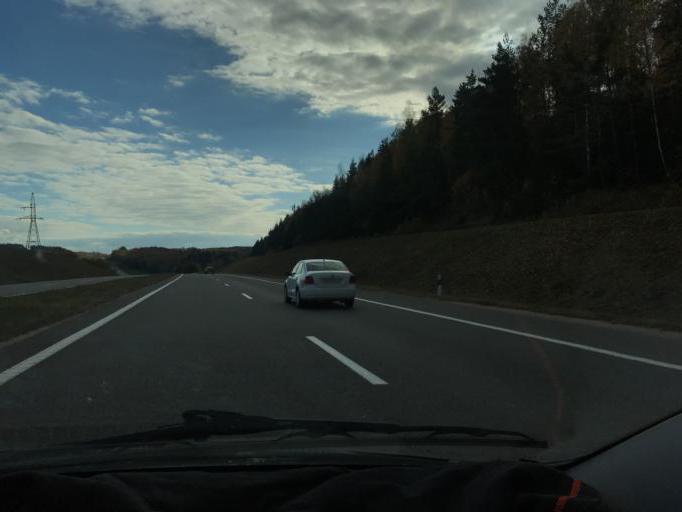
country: BY
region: Minsk
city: Lahoysk
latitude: 54.1938
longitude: 27.8157
